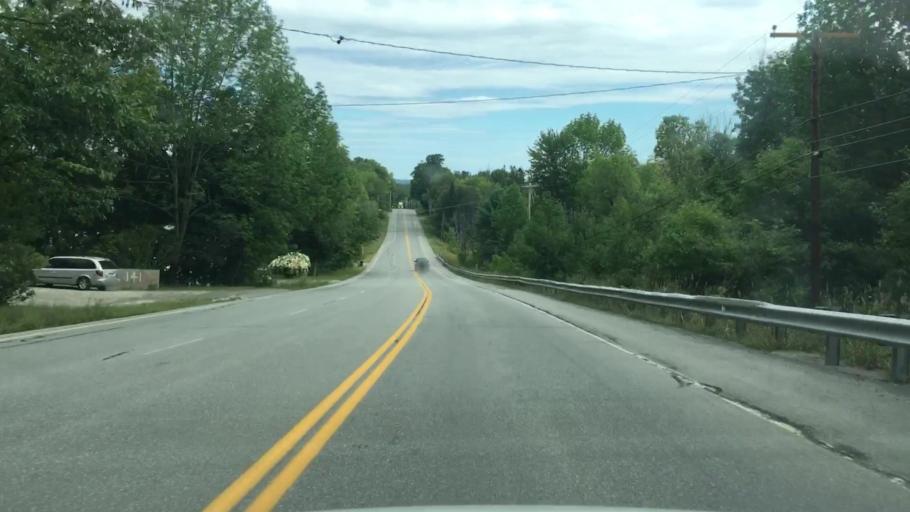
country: US
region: Maine
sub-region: Piscataquis County
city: Milo
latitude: 45.2453
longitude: -69.0057
